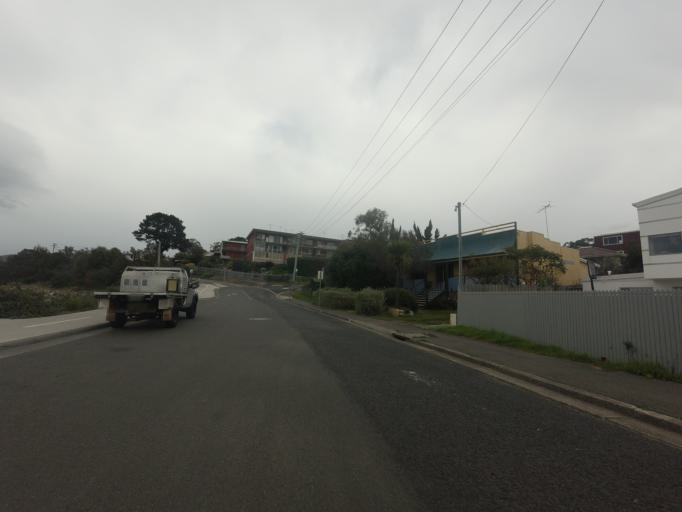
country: AU
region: Tasmania
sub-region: Clarence
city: Bellerive
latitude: -42.8791
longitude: 147.3707
